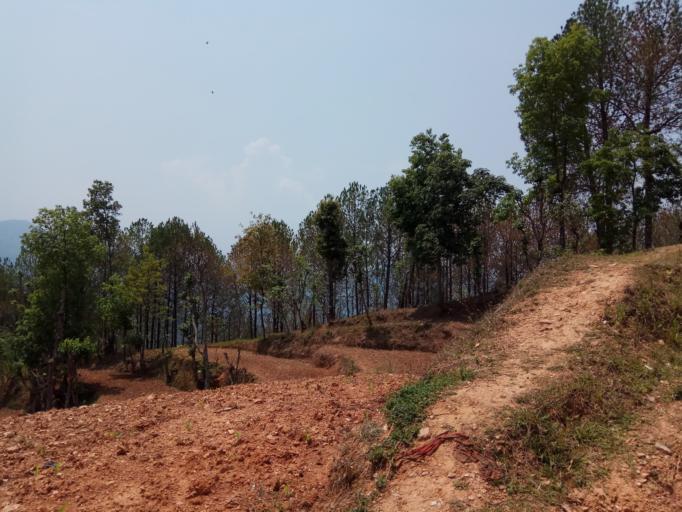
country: NP
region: Central Region
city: Kirtipur
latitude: 27.8929
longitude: 85.0796
